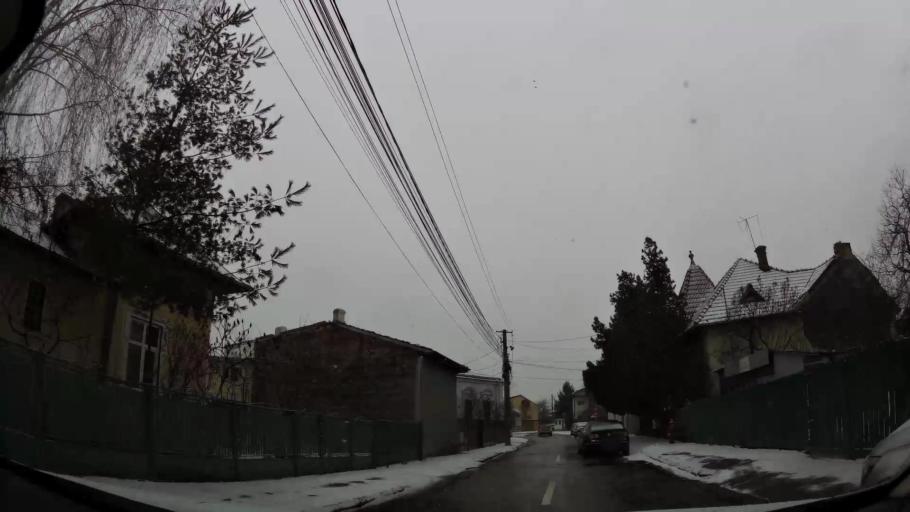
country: RO
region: Dambovita
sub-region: Municipiul Targoviste
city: Targoviste
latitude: 44.9270
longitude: 25.4554
